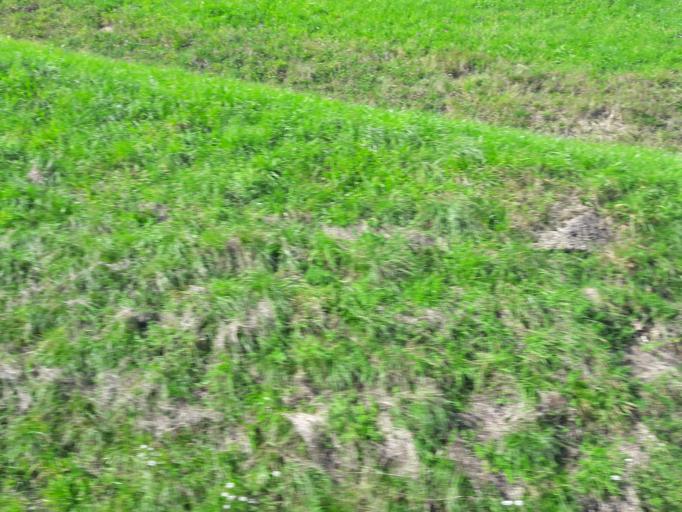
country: CH
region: Schwyz
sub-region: Bezirk Schwyz
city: Sattel
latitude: 47.0711
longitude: 8.6197
